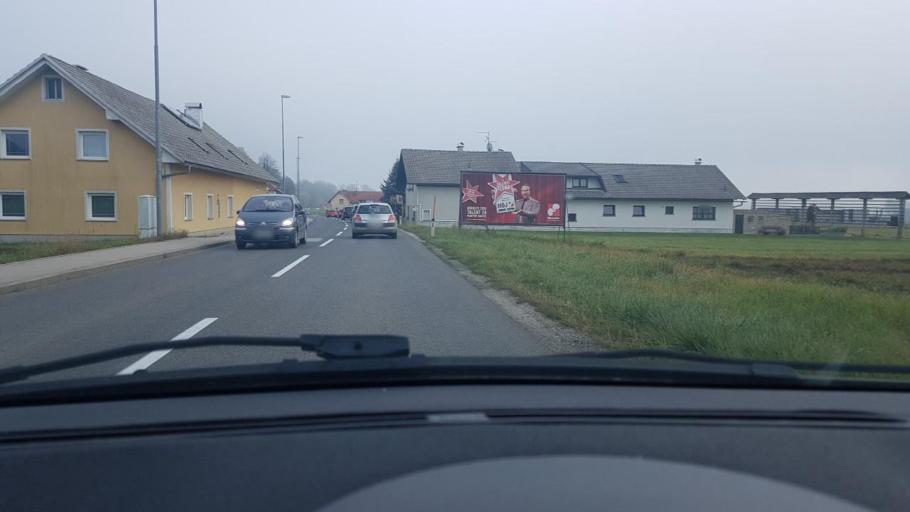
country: SI
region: Cerklje na Gorenjskem
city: Cerklje na Gorenjskem
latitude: 46.2261
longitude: 14.4893
